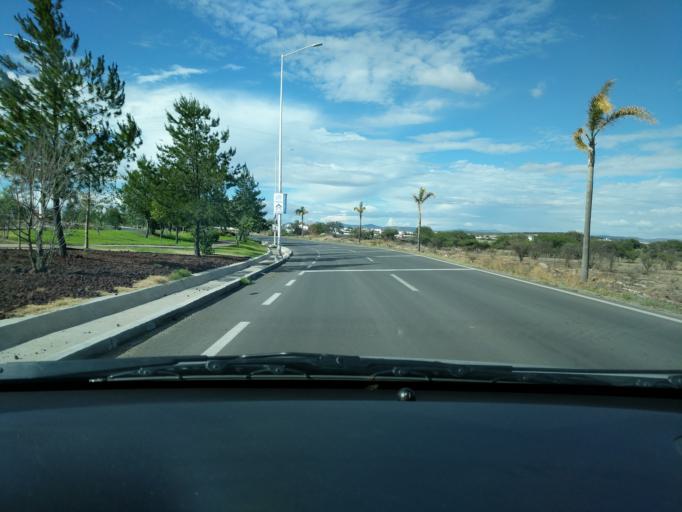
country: MX
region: Queretaro
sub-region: El Marques
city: Paseos del Marques
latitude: 20.5940
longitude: -100.2769
